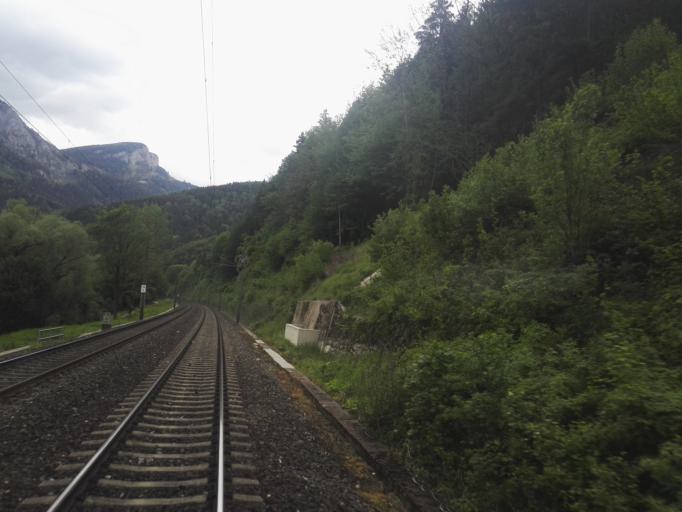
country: AT
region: Styria
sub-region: Politischer Bezirk Graz-Umgebung
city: Rothelstein
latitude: 47.3032
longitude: 15.3728
